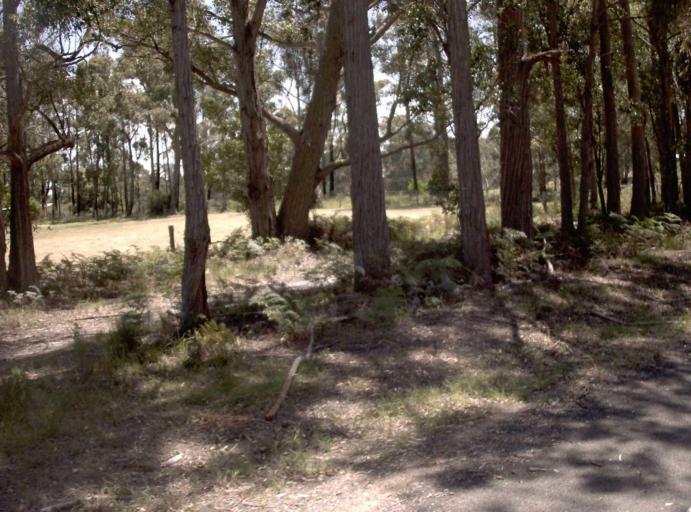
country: AU
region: Victoria
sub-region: East Gippsland
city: Lakes Entrance
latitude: -37.7779
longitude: 148.0504
